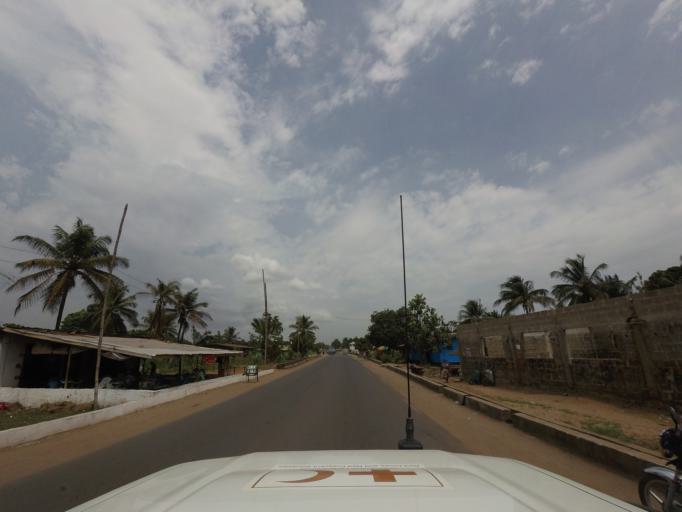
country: LR
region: Montserrado
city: Monrovia
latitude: 6.2842
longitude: -10.6863
